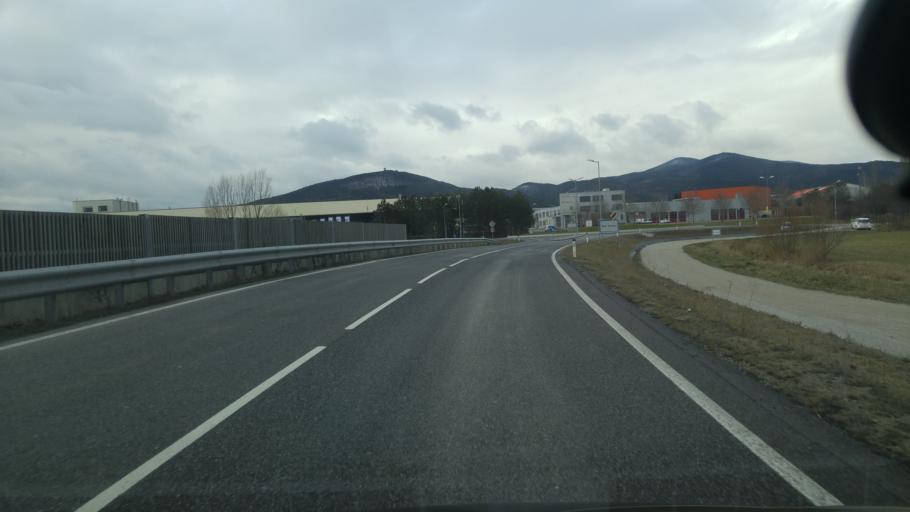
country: AT
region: Lower Austria
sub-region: Politischer Bezirk Baden
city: Bad Voslau
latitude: 47.9746
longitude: 16.2290
